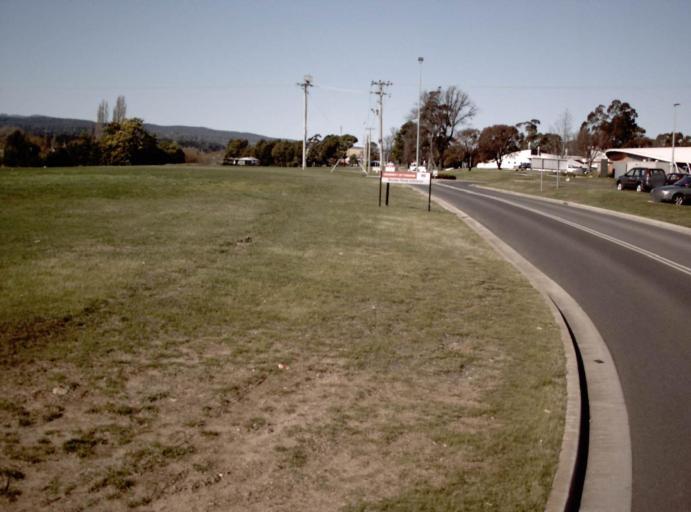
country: AU
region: Tasmania
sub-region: Launceston
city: Newnham
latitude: -41.3975
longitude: 147.1202
